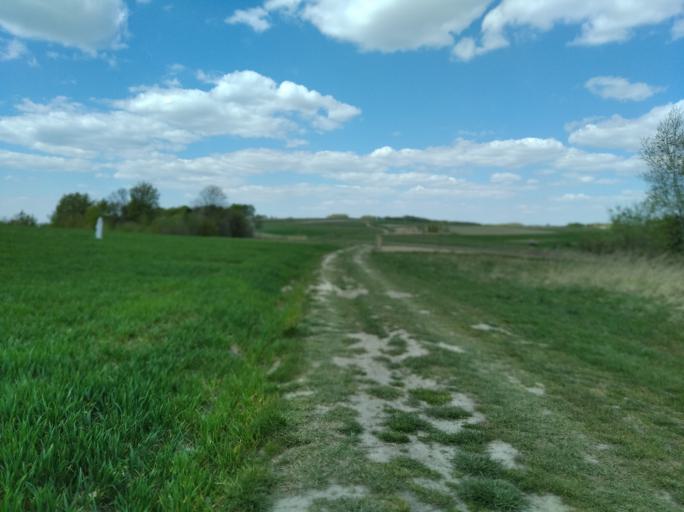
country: PL
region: Subcarpathian Voivodeship
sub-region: Powiat brzozowski
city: Golcowa
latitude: 49.7561
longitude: 22.0713
